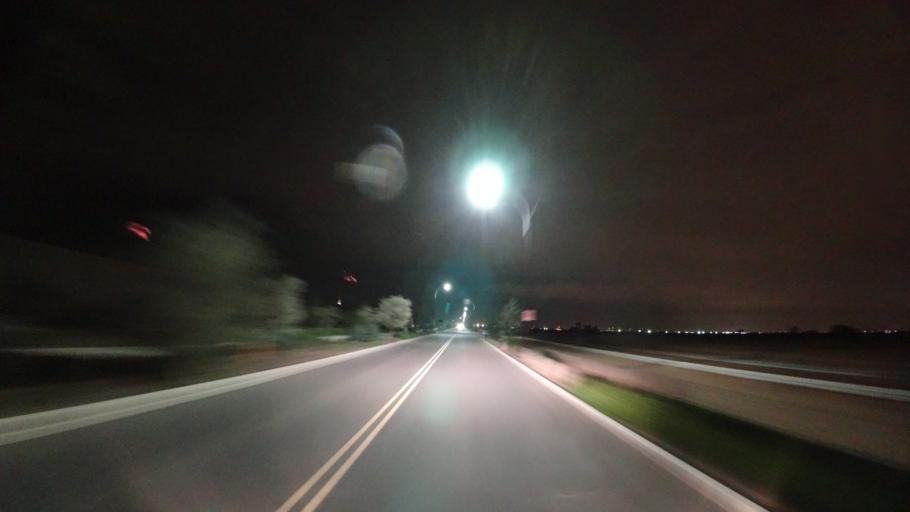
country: US
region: Arizona
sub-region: Maricopa County
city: Queen Creek
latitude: 33.3346
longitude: -111.6073
